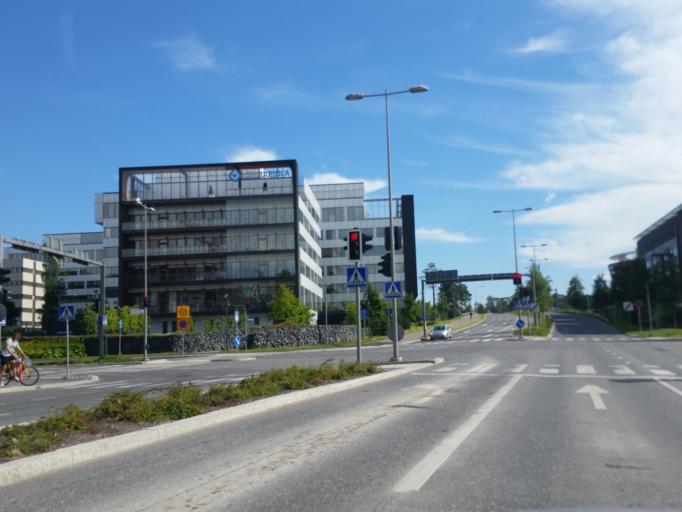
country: FI
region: Uusimaa
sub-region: Helsinki
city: Otaniemi
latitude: 60.1719
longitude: 24.8021
